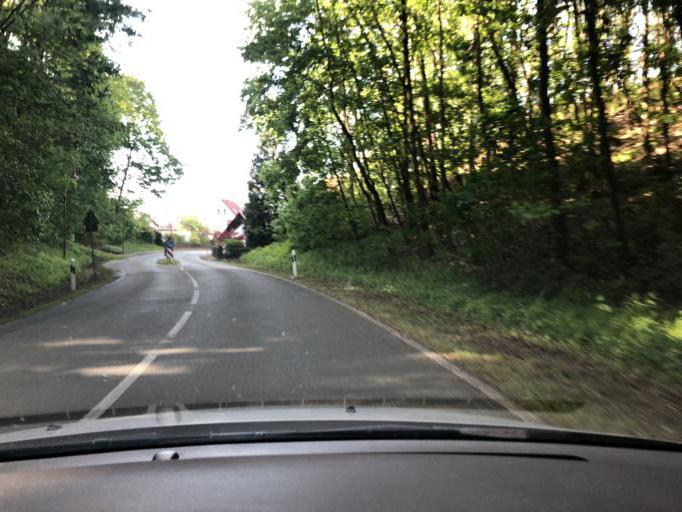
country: DE
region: Thuringia
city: Haselbach
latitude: 51.0660
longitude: 12.4380
